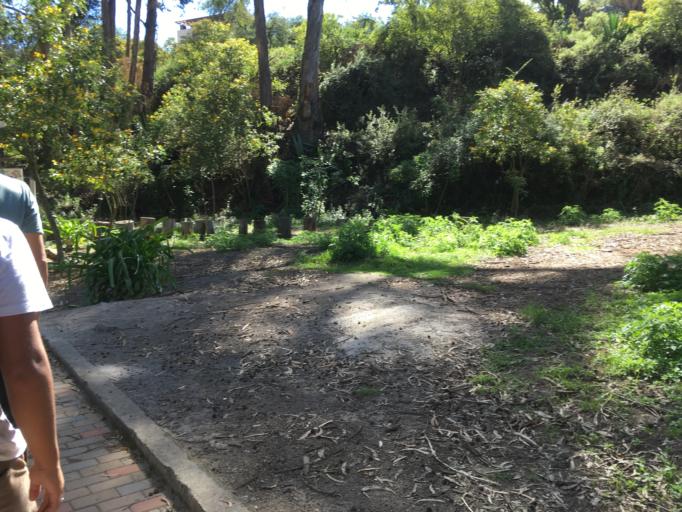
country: EC
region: Tungurahua
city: Ambato
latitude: -1.2466
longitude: -78.6372
